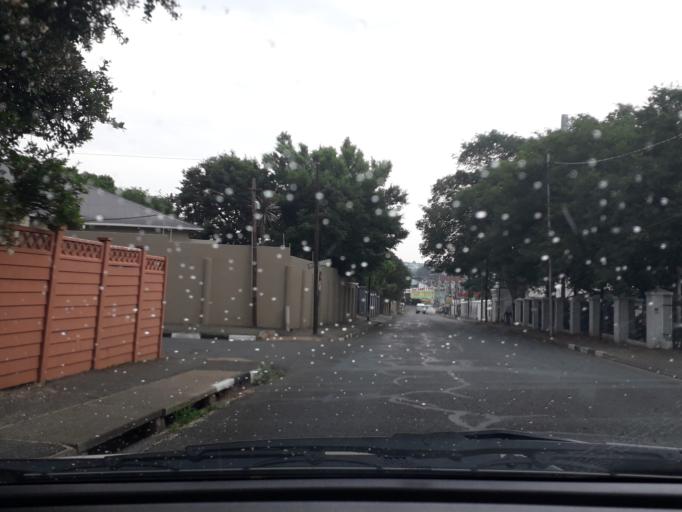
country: ZA
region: Gauteng
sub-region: City of Johannesburg Metropolitan Municipality
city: Johannesburg
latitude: -26.1543
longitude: 28.0875
